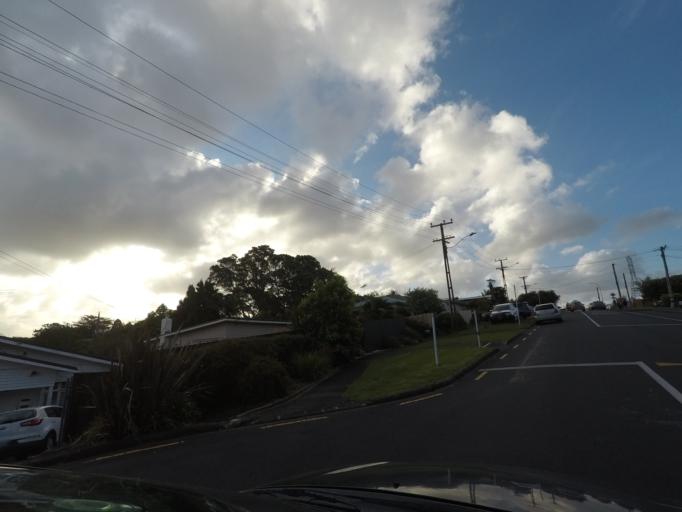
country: NZ
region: Auckland
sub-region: Auckland
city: Auckland
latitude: -36.9226
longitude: 174.7566
